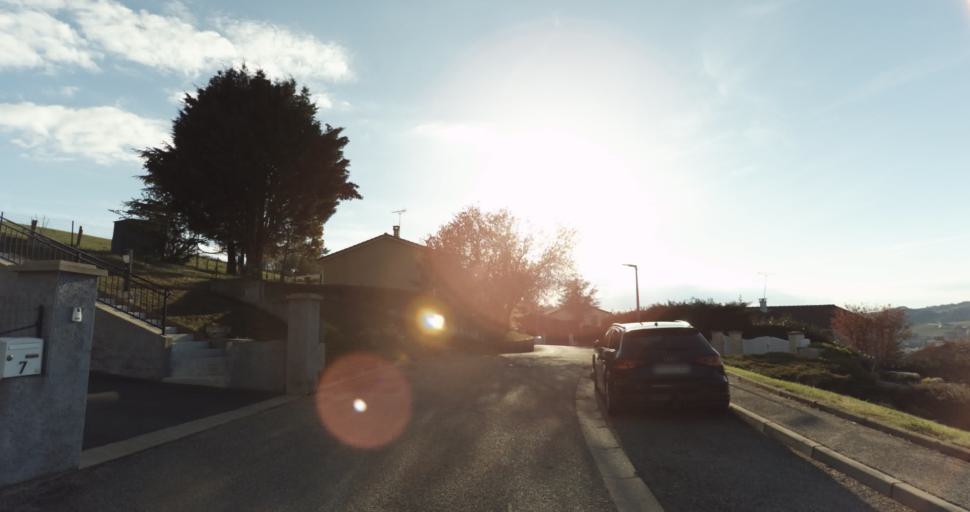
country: FR
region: Rhone-Alpes
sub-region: Departement de la Loire
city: Saint-Jean-Bonnefonds
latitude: 45.4663
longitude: 4.4466
